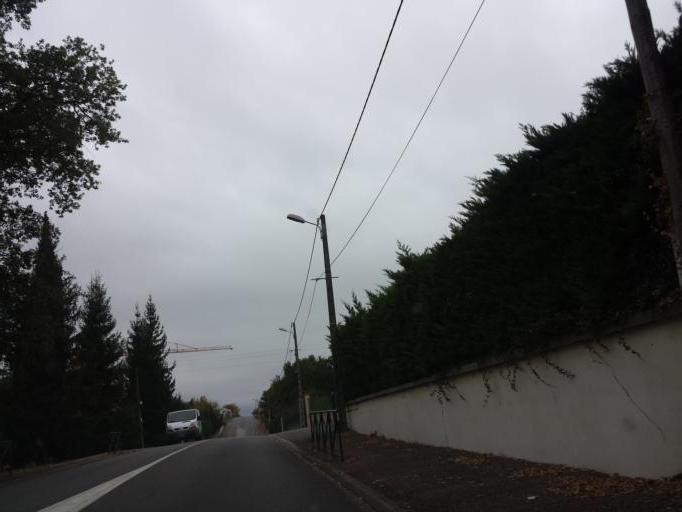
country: FR
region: Poitou-Charentes
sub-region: Departement de la Charente
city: Puymoyen
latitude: 45.6218
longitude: 0.1651
